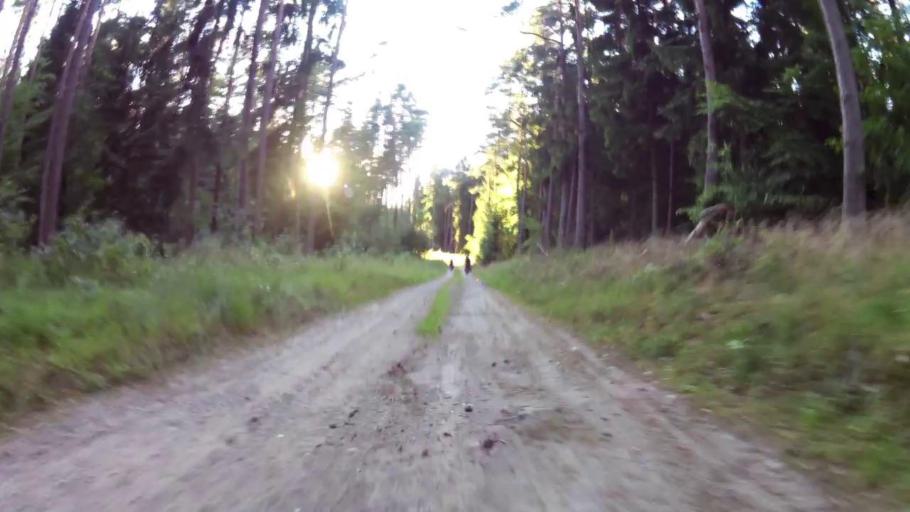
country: PL
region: West Pomeranian Voivodeship
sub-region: Powiat lobeski
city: Lobez
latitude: 53.7460
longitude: 15.6453
